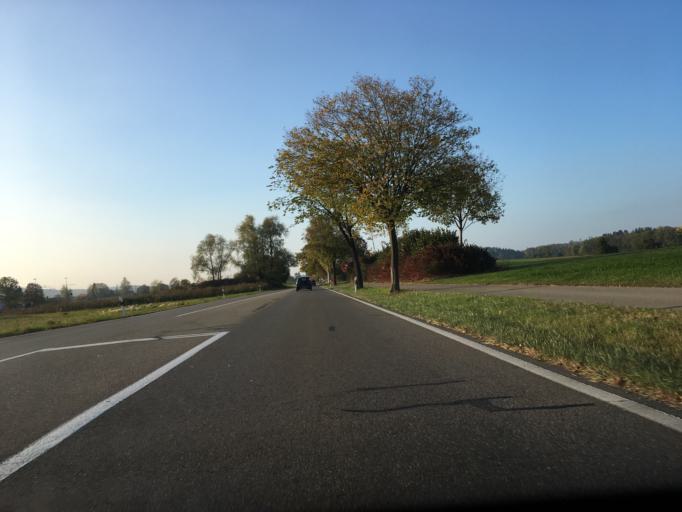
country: CH
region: Zurich
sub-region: Bezirk Pfaeffikon
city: Pfaeffikon / Pfaeffikon (Dorfkern)
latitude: 47.3731
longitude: 8.7732
